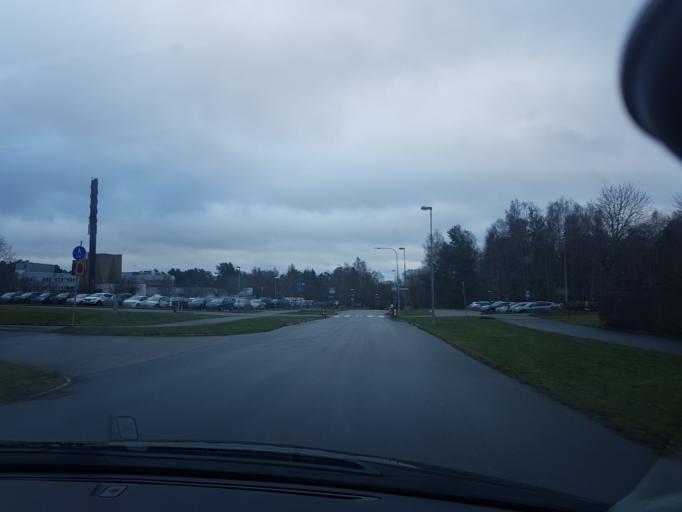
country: SE
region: Joenkoeping
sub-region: Vetlanda Kommun
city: Vetlanda
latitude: 57.4345
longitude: 15.0797
